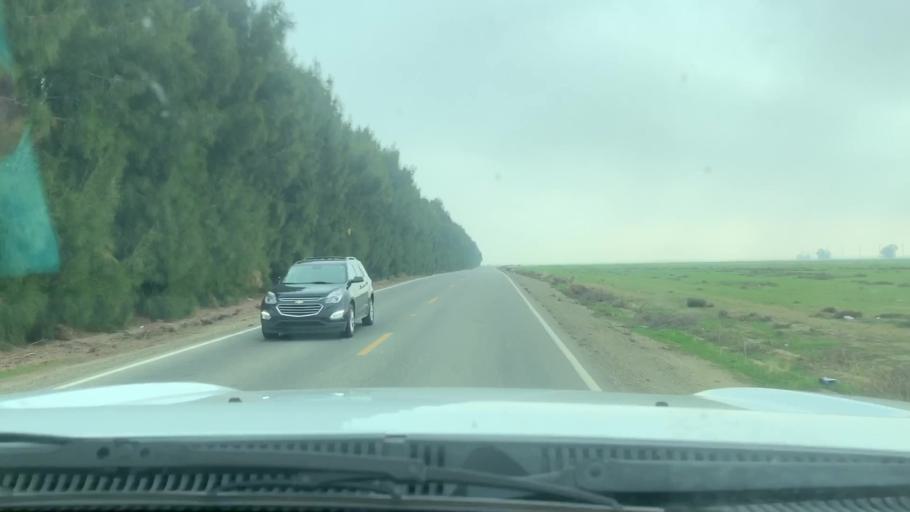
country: US
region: California
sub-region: Kern County
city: Lost Hills
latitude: 35.5204
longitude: -119.7552
